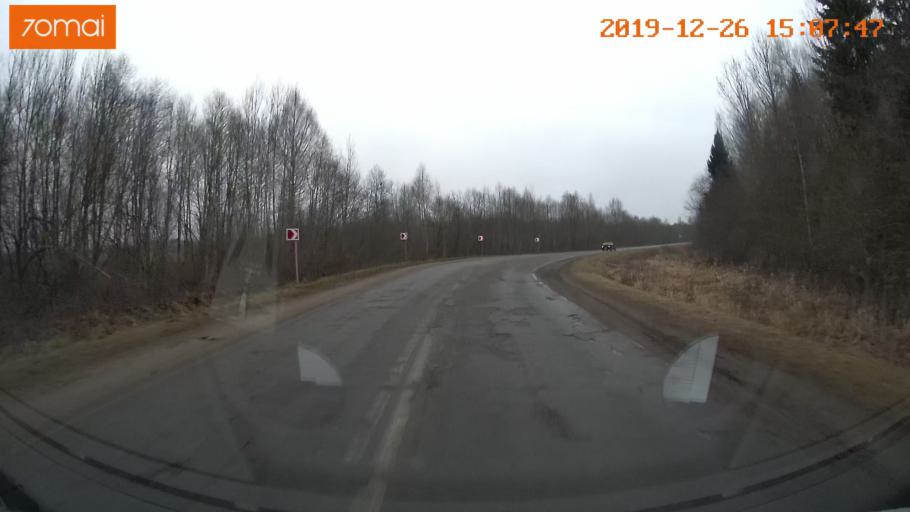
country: RU
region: Jaroslavl
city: Rybinsk
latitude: 58.1663
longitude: 38.8423
